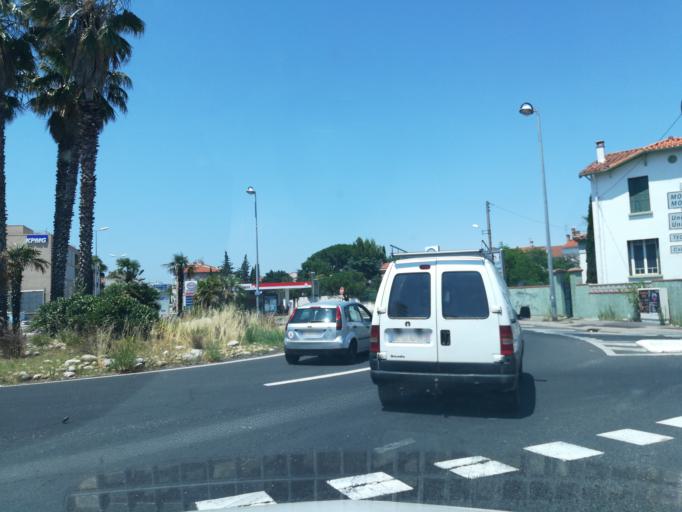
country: FR
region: Languedoc-Roussillon
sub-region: Departement des Pyrenees-Orientales
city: Perpignan
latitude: 42.6884
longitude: 2.8951
